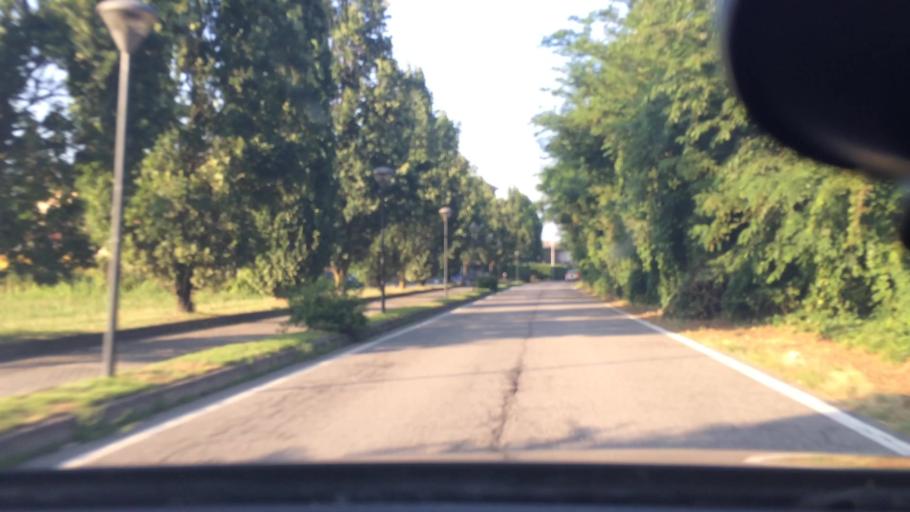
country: IT
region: Lombardy
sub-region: Citta metropolitana di Milano
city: Mantegazza
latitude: 45.5099
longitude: 8.9679
